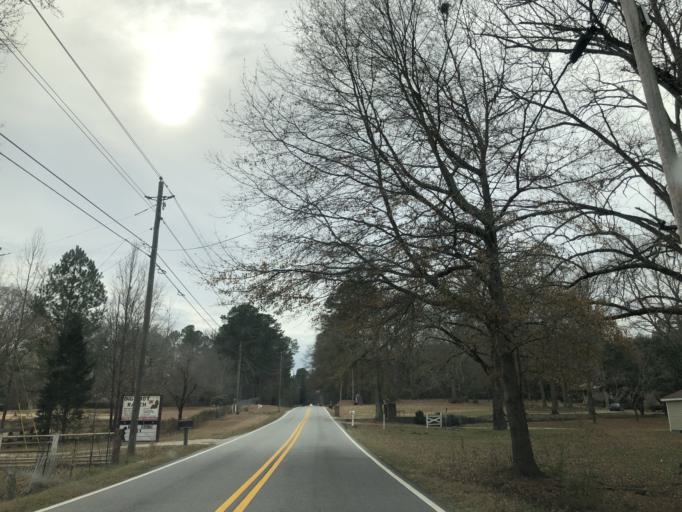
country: US
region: Georgia
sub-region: DeKalb County
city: Panthersville
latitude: 33.6402
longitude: -84.2083
